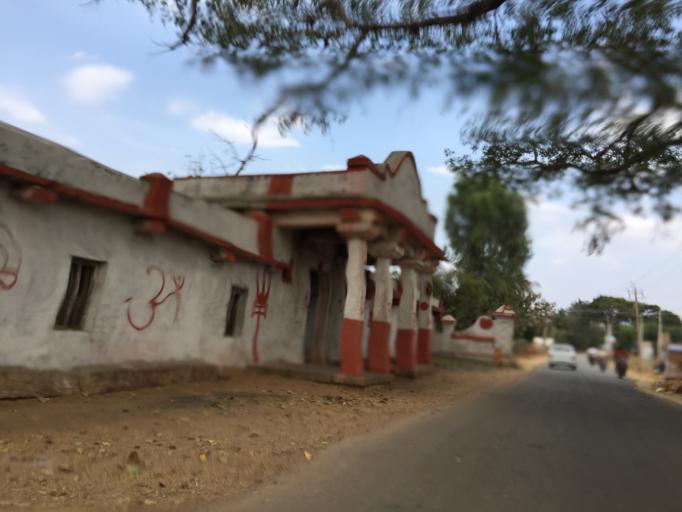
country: IN
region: Karnataka
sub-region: Chikkaballapur
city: Chik Ballapur
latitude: 13.3841
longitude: 77.6865
